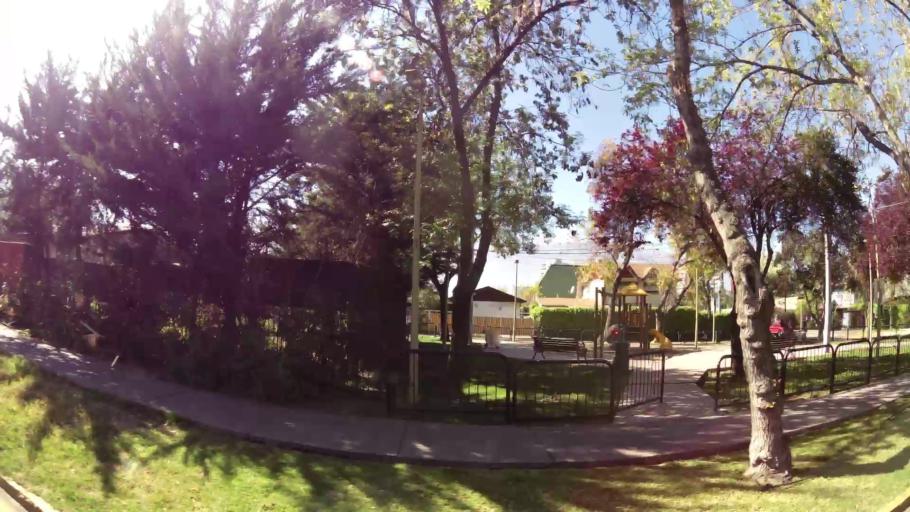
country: CL
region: Santiago Metropolitan
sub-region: Provincia de Santiago
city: Villa Presidente Frei, Nunoa, Santiago, Chile
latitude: -33.4042
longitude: -70.5535
